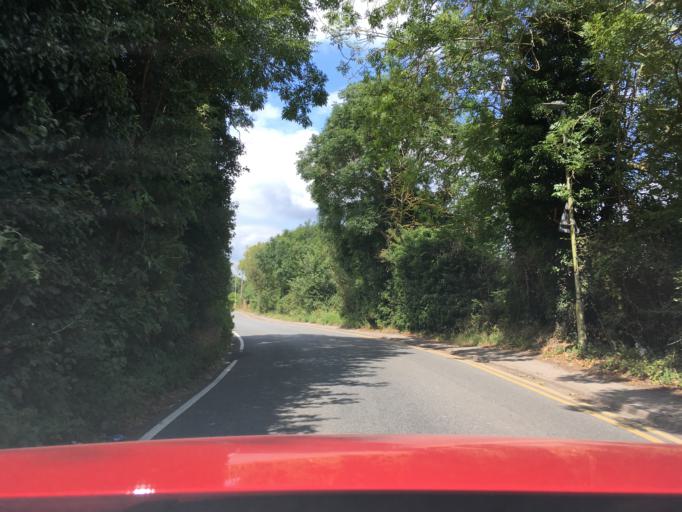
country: GB
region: England
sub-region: Gloucestershire
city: Gloucester
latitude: 51.8787
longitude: -2.2435
